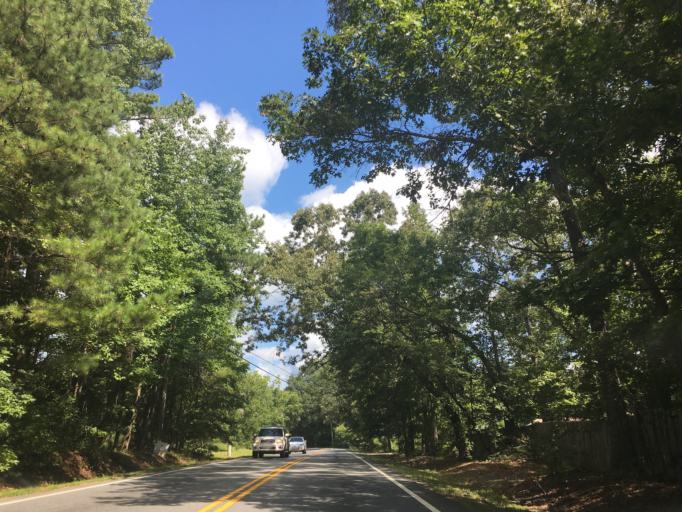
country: US
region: Georgia
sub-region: Fulton County
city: Roswell
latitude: 34.0925
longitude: -84.3628
